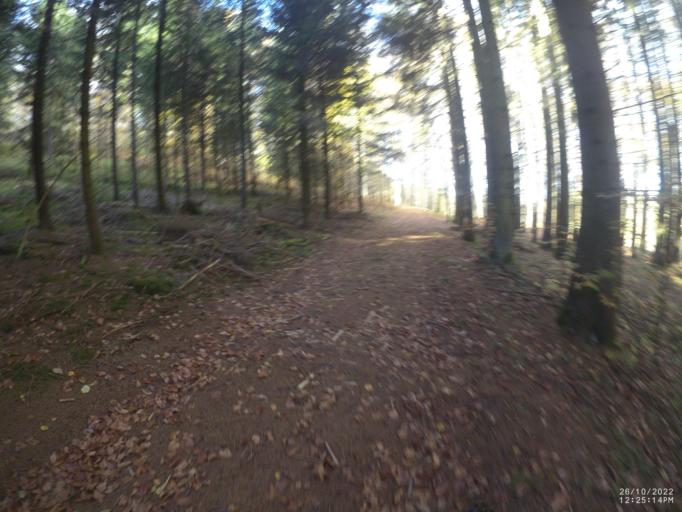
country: DE
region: Baden-Wuerttemberg
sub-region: Regierungsbezirk Stuttgart
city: Wiesensteig
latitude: 48.5425
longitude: 9.6119
